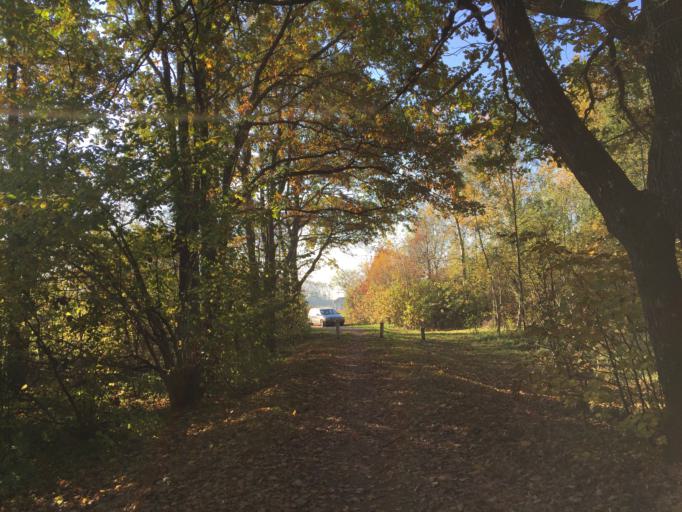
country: LT
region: Klaipedos apskritis
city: Kretinga
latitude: 55.8936
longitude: 21.2092
